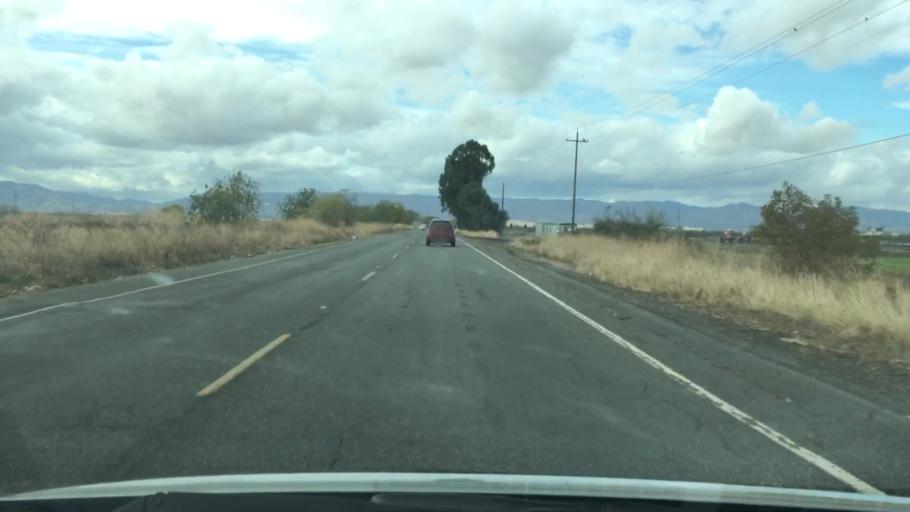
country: US
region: California
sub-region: Yolo County
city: Winters
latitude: 38.5616
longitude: -121.8909
